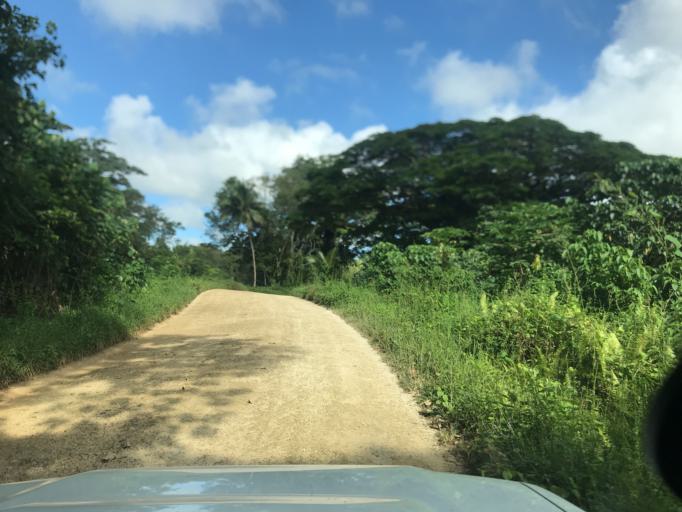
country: VU
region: Sanma
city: Luganville
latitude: -15.5103
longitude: 167.1200
